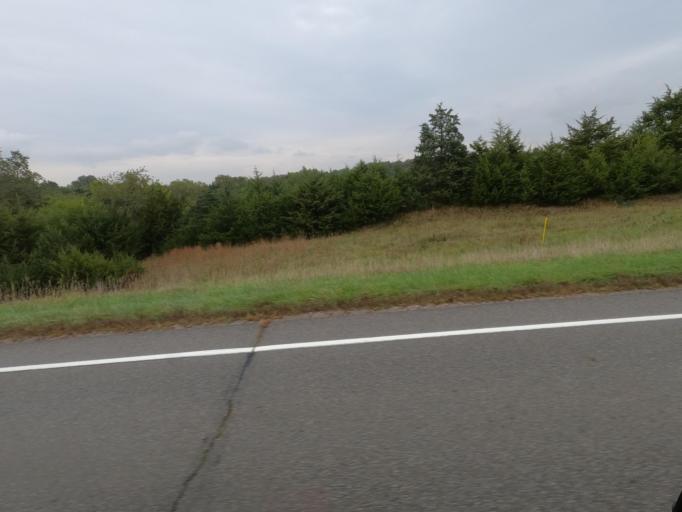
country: US
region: Iowa
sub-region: Van Buren County
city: Keosauqua
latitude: 40.8091
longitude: -91.9243
